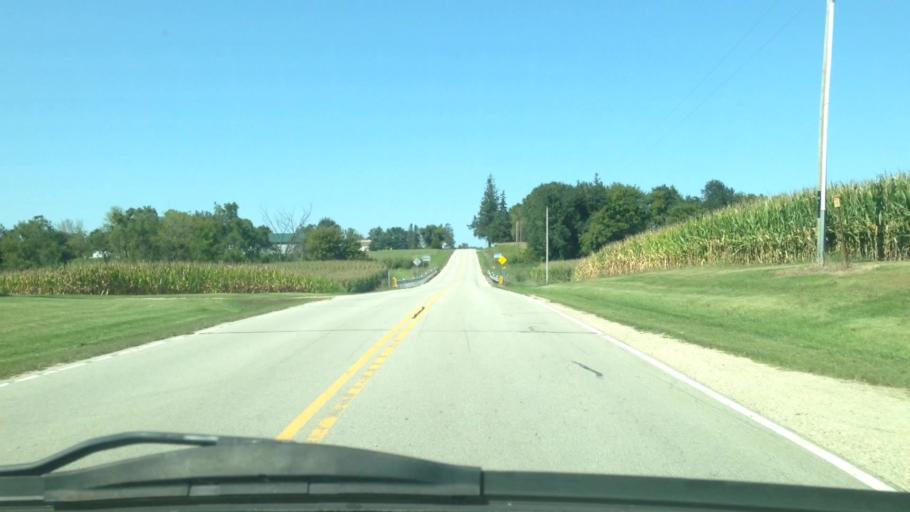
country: US
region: Minnesota
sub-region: Fillmore County
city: Rushford
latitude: 43.7042
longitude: -91.7704
